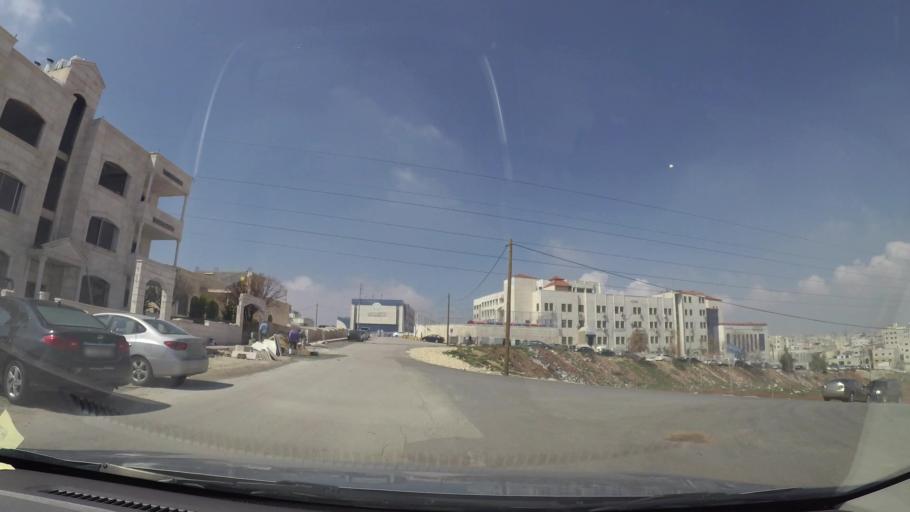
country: JO
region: Amman
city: Al Bunayyat ash Shamaliyah
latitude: 31.8890
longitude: 35.8966
